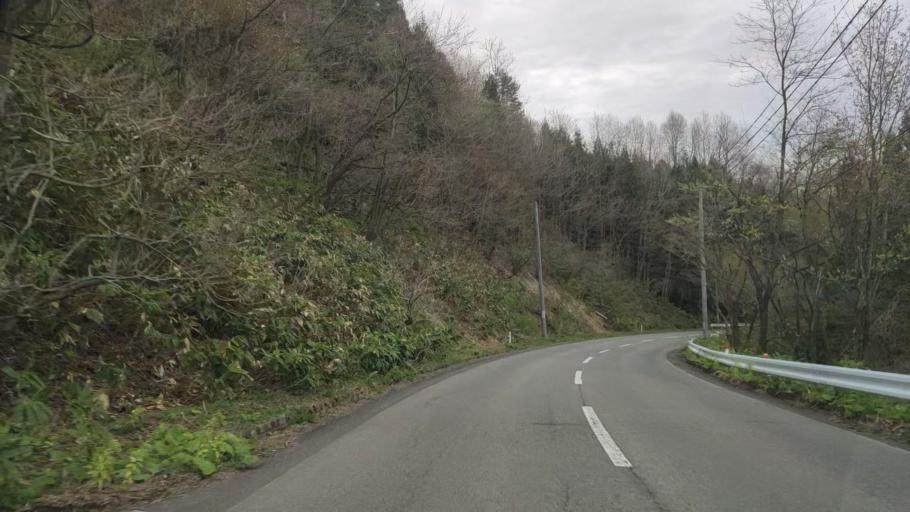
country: JP
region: Akita
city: Hanawa
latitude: 40.3680
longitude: 140.7846
